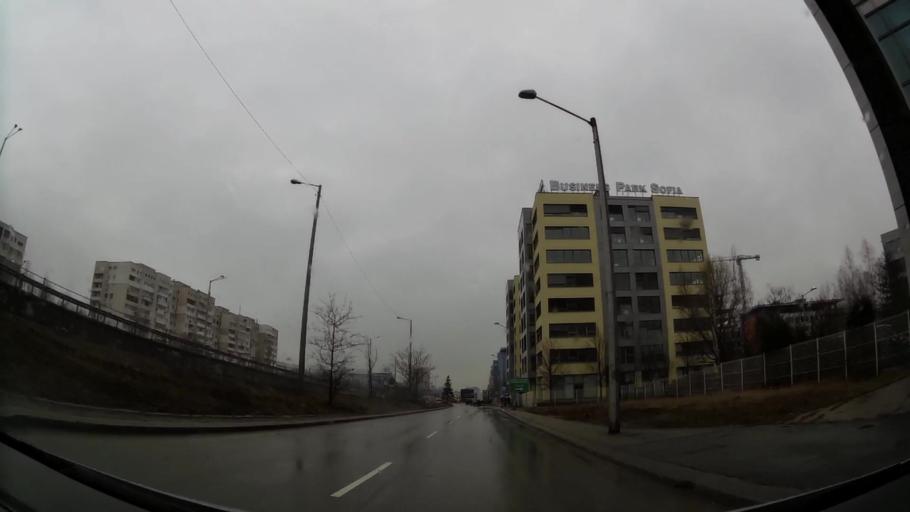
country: BG
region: Sofia-Capital
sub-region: Stolichna Obshtina
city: Sofia
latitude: 42.6275
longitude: 23.3733
